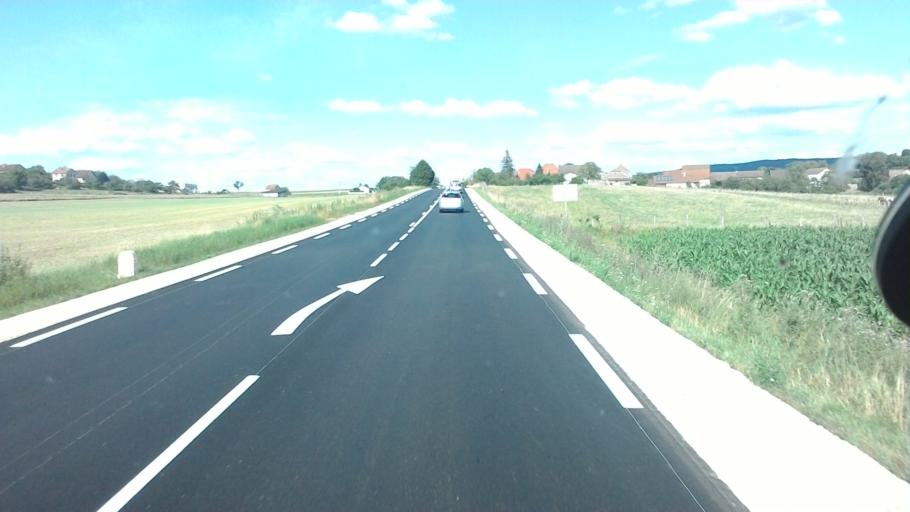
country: FR
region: Franche-Comte
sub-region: Departement de la Haute-Saone
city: Gy
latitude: 47.4286
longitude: 5.8547
